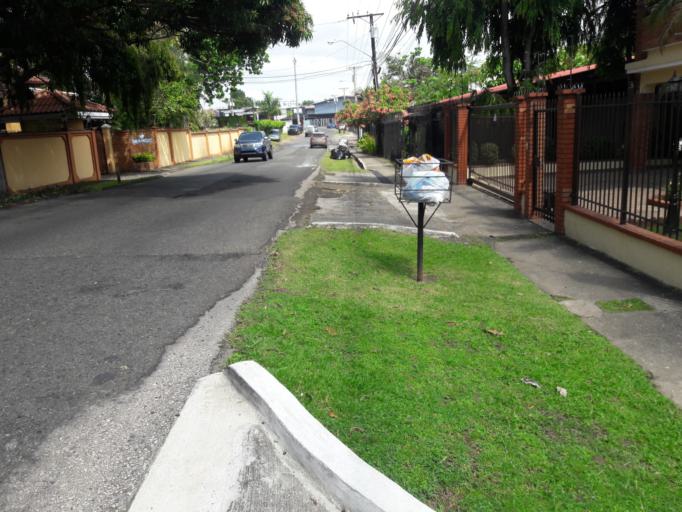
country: PA
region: Panama
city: Panama
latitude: 9.0038
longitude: -79.5022
